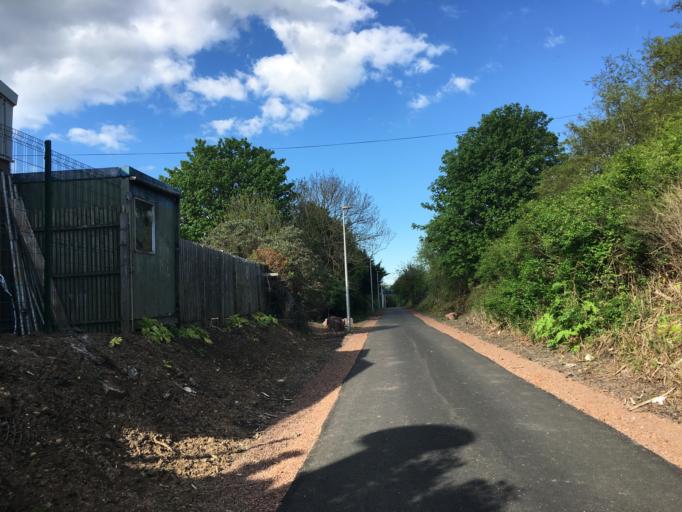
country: GB
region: Scotland
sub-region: Midlothian
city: Bonnyrigg
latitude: 55.9002
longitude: -3.1265
